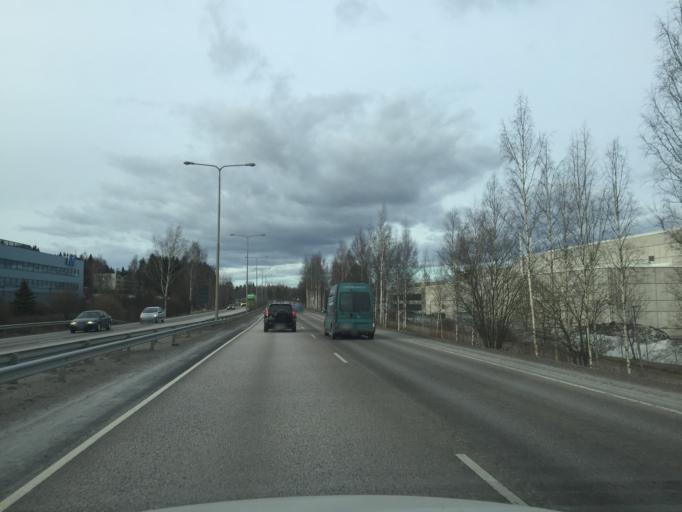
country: FI
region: Uusimaa
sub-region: Helsinki
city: Teekkarikylae
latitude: 60.2672
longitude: 24.8750
